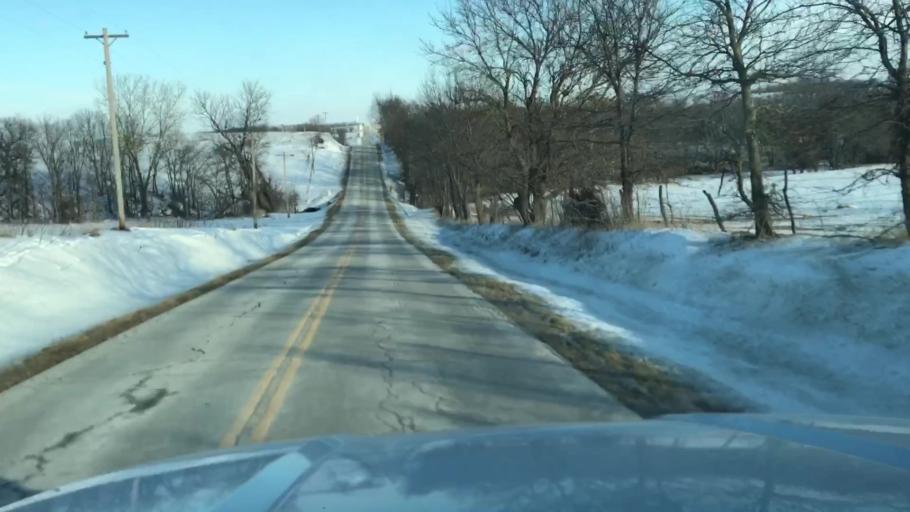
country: US
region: Missouri
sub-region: Andrew County
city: Savannah
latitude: 40.0246
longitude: -94.9112
